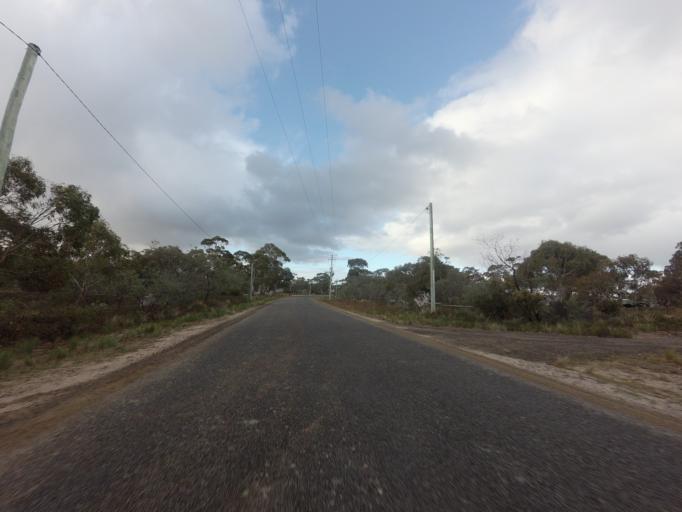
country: AU
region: Tasmania
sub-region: Break O'Day
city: St Helens
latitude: -42.1025
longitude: 148.0800
